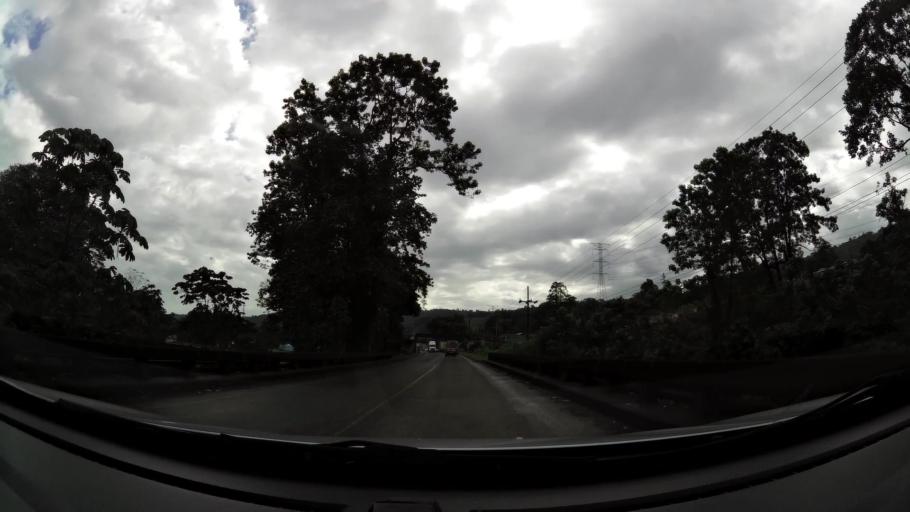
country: CR
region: Limon
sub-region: Canton de Siquirres
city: Siquirres
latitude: 10.0939
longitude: -83.5091
